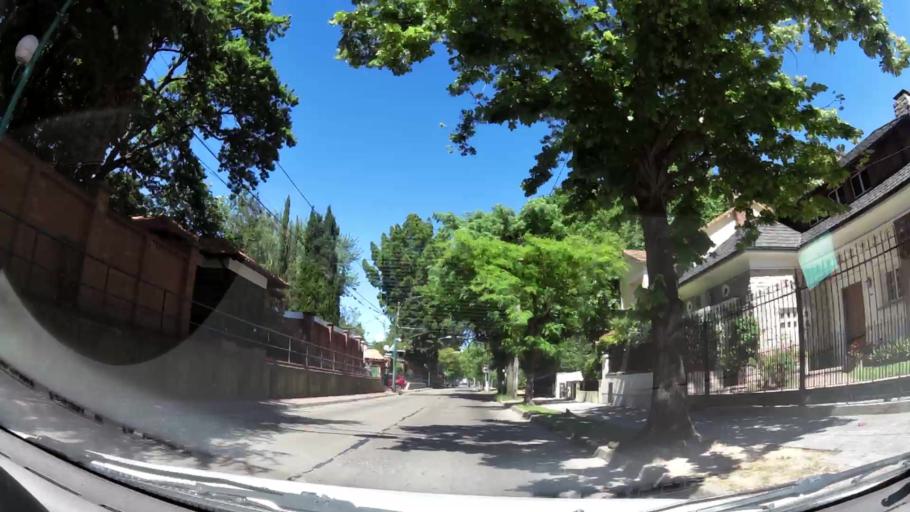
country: AR
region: Buenos Aires
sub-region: Partido de Vicente Lopez
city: Olivos
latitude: -34.5130
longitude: -58.4822
